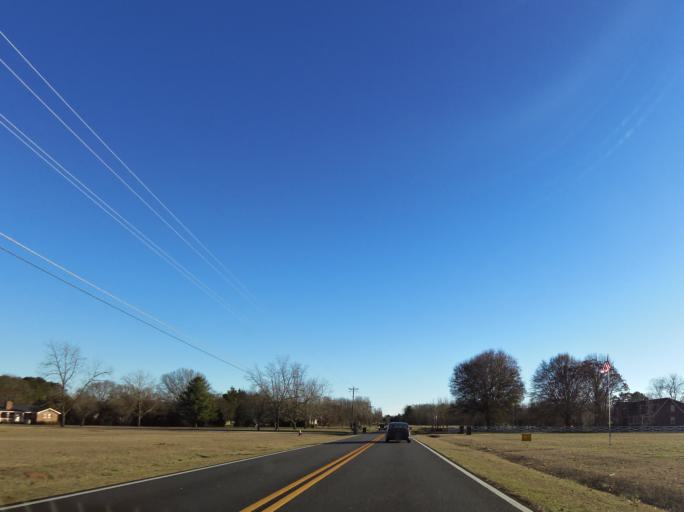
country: US
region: Georgia
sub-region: Houston County
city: Centerville
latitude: 32.6553
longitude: -83.6969
